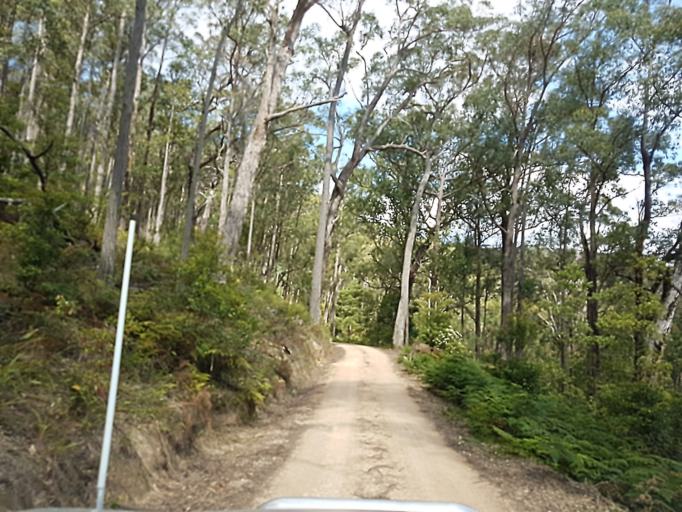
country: AU
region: Victoria
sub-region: East Gippsland
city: Lakes Entrance
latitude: -37.4064
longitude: 148.2334
